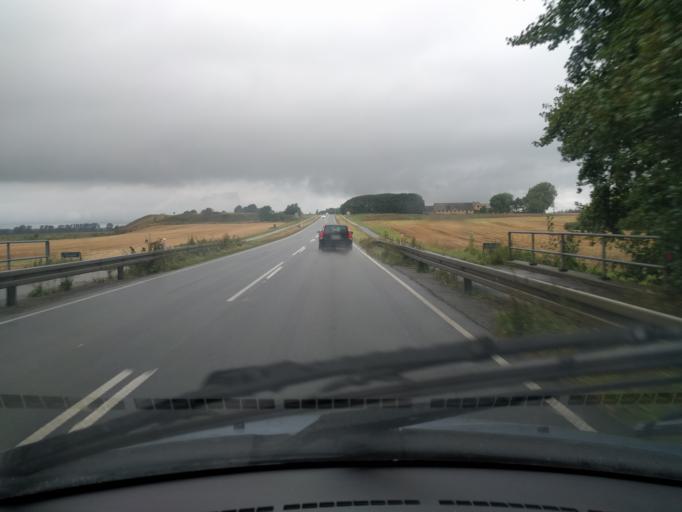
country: DK
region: Zealand
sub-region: Naestved Kommune
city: Naestved
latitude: 55.1399
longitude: 11.8188
